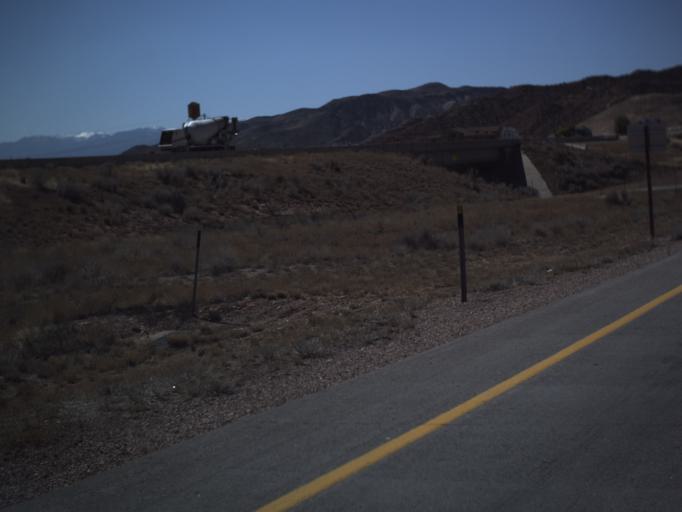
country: US
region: Utah
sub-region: Sevier County
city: Richfield
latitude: 38.7911
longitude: -112.0818
